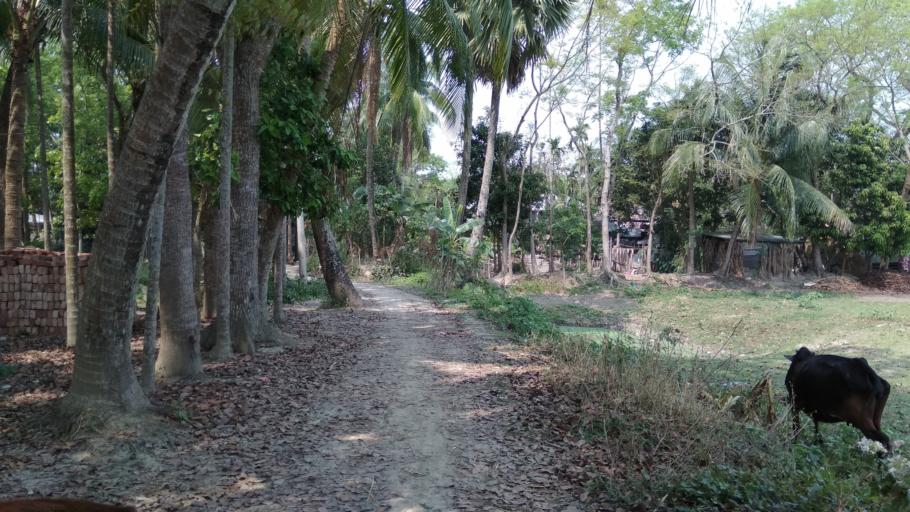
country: BD
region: Barisal
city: Mehendiganj
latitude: 22.9368
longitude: 90.4138
